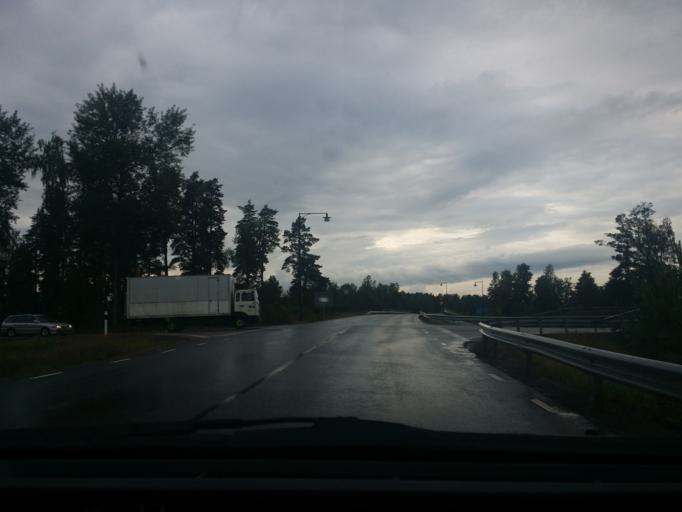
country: SE
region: Vaestmanland
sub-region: Arboga Kommun
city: Arboga
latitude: 59.4233
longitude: 15.8262
